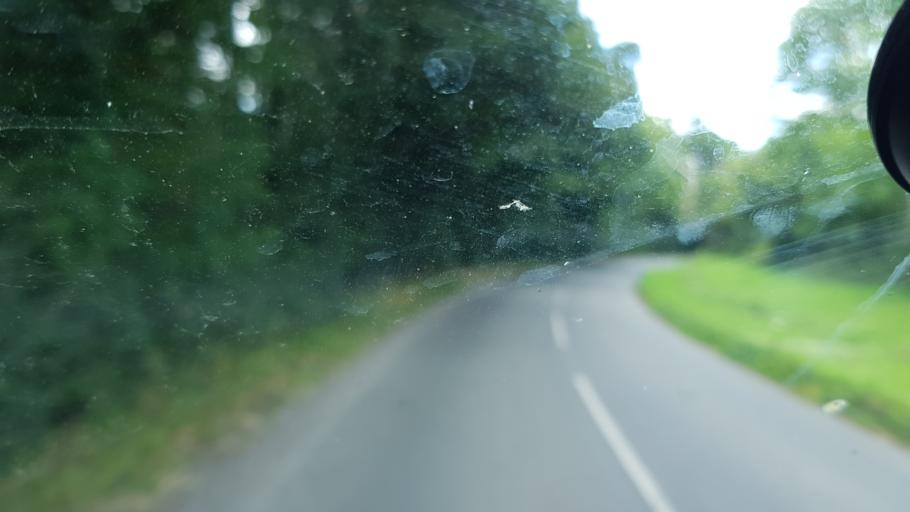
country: GB
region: England
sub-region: West Sussex
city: Rudgwick
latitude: 51.0748
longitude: -0.4528
